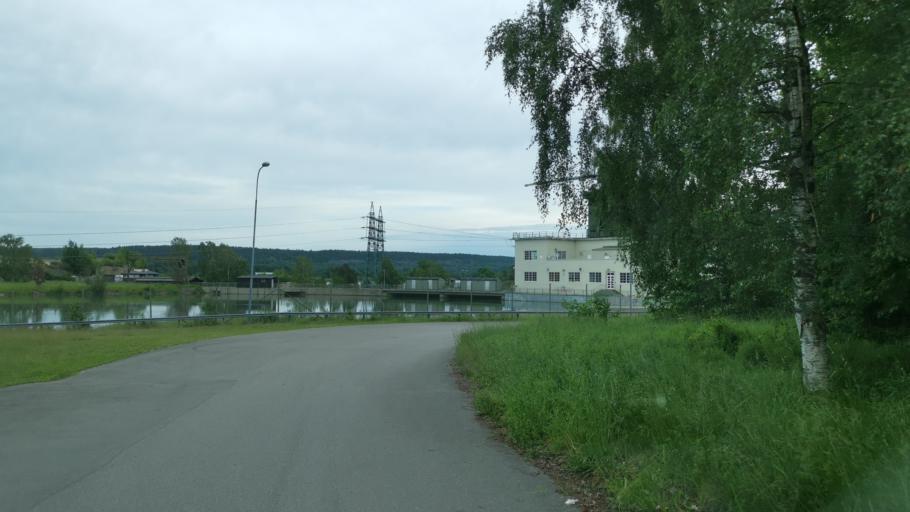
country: SE
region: Vaestra Goetaland
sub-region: Vanersborgs Kommun
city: Vargon
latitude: 58.3570
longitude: 12.3725
